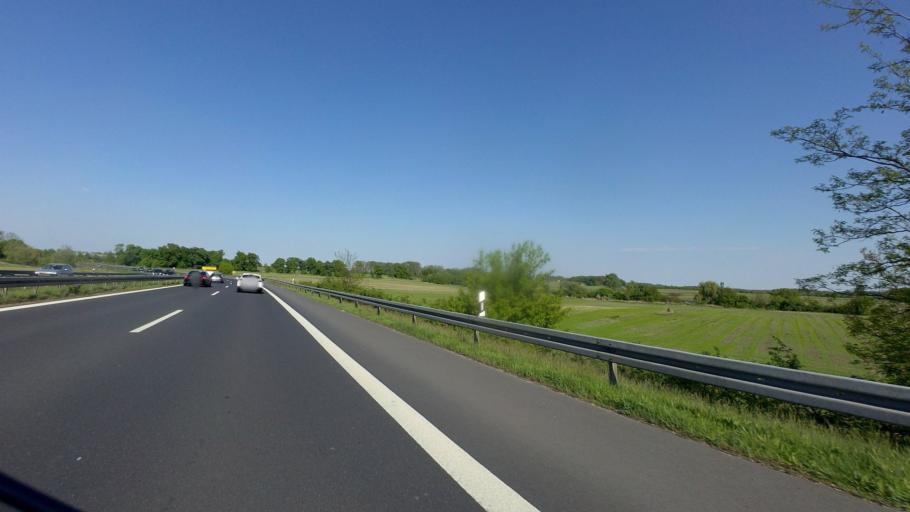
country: DE
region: Brandenburg
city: Grossbeeren
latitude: 52.3836
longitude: 13.3321
